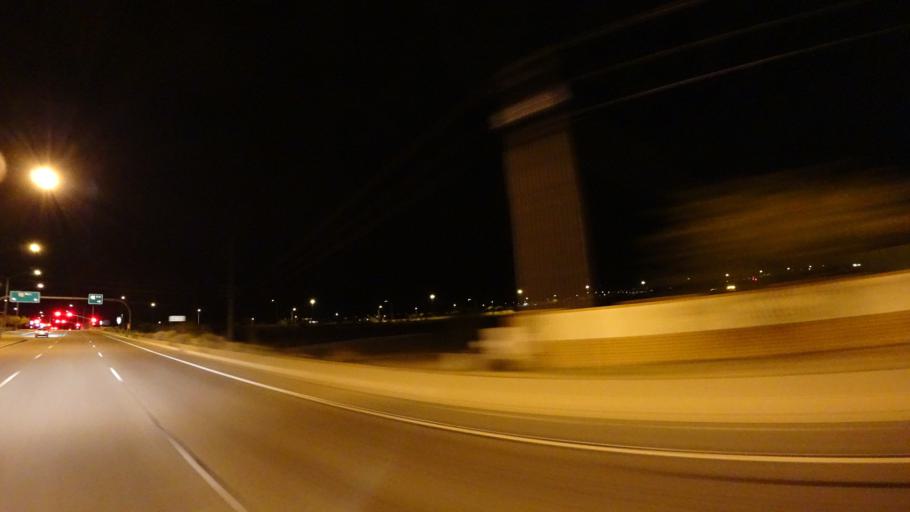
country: US
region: Arizona
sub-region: Maricopa County
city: Mesa
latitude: 33.4791
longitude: -111.7184
